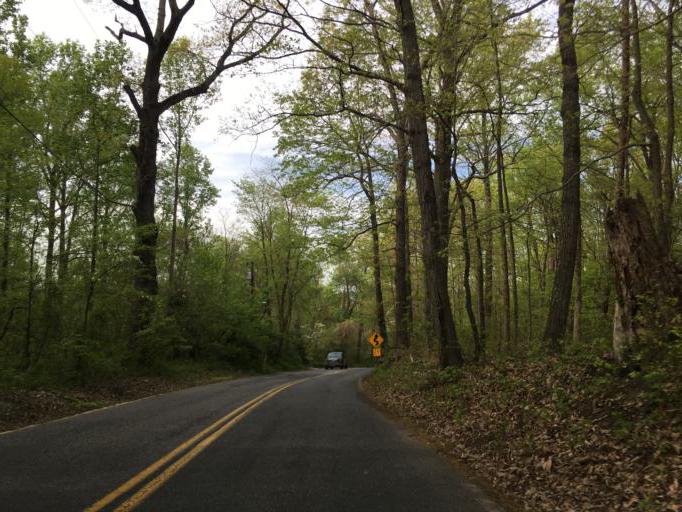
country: US
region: Maryland
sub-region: Howard County
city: Elkridge
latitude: 39.2048
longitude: -76.7035
